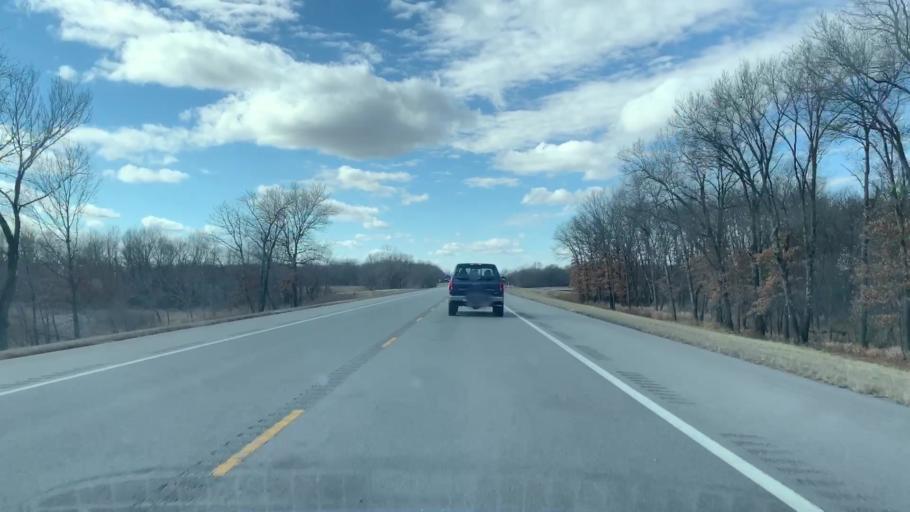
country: US
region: Kansas
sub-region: Cherokee County
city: Columbus
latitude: 37.3401
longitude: -94.9752
